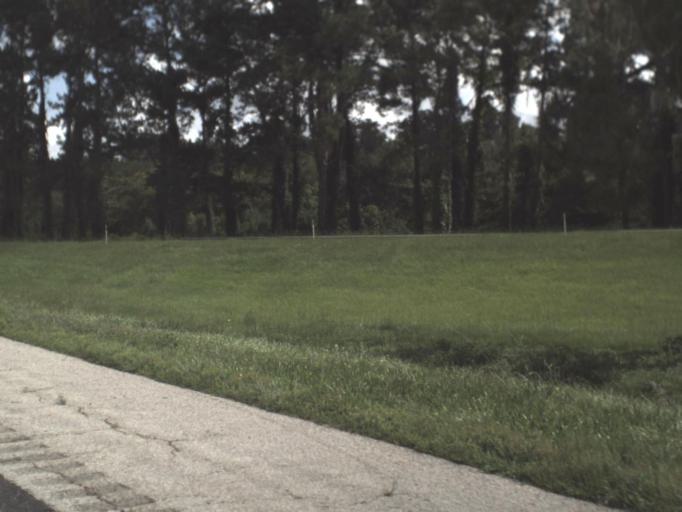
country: US
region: Florida
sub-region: Alachua County
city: High Springs
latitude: 29.8768
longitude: -82.5428
